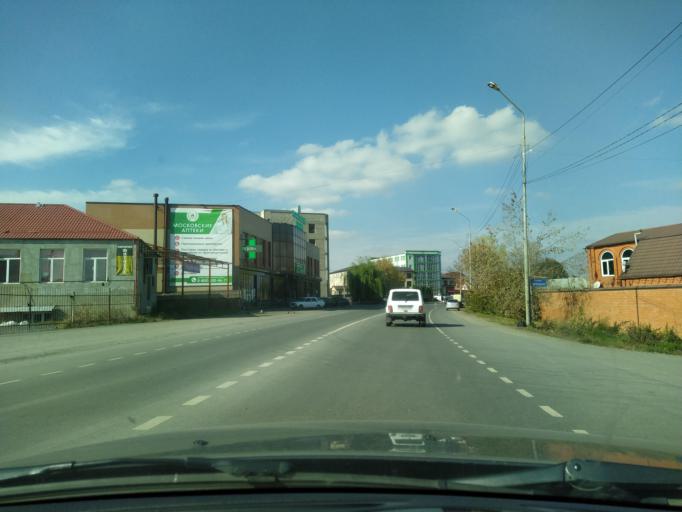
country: RU
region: Ingushetiya
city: Magas
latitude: 43.1980
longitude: 44.7566
